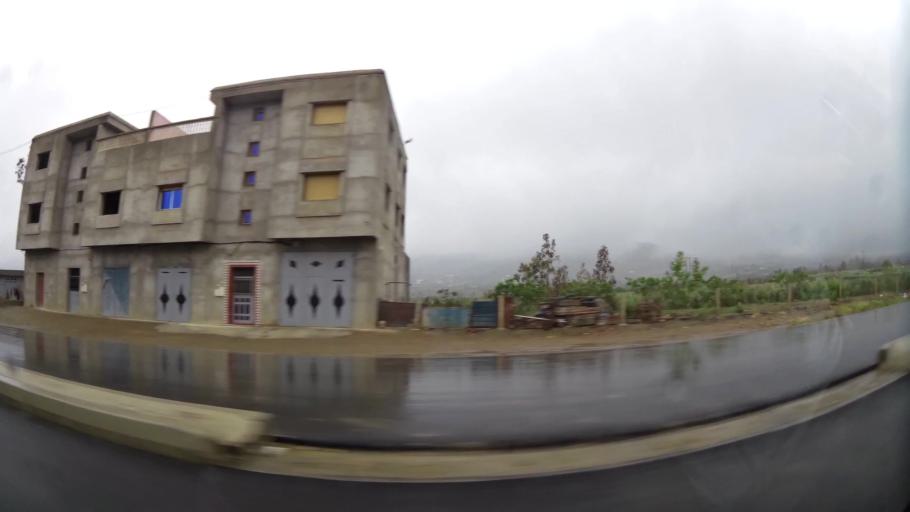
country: MA
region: Taza-Al Hoceima-Taounate
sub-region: Taza
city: Aknoul
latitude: 34.8228
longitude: -3.7242
